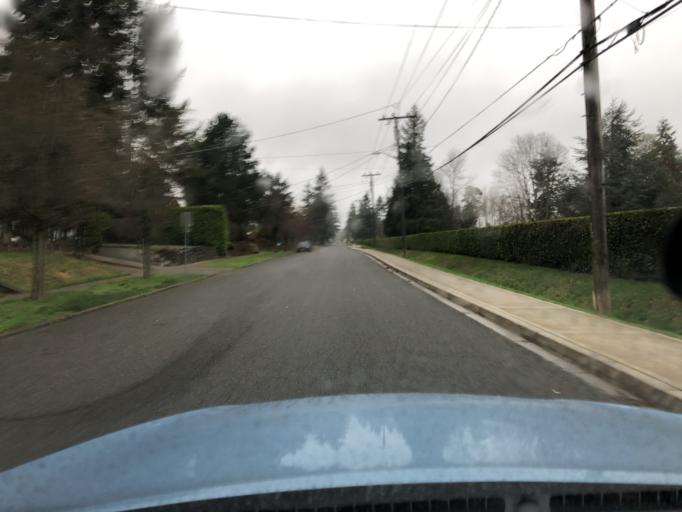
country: US
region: Washington
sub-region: King County
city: Lake Forest Park
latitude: 47.7378
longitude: -122.2993
